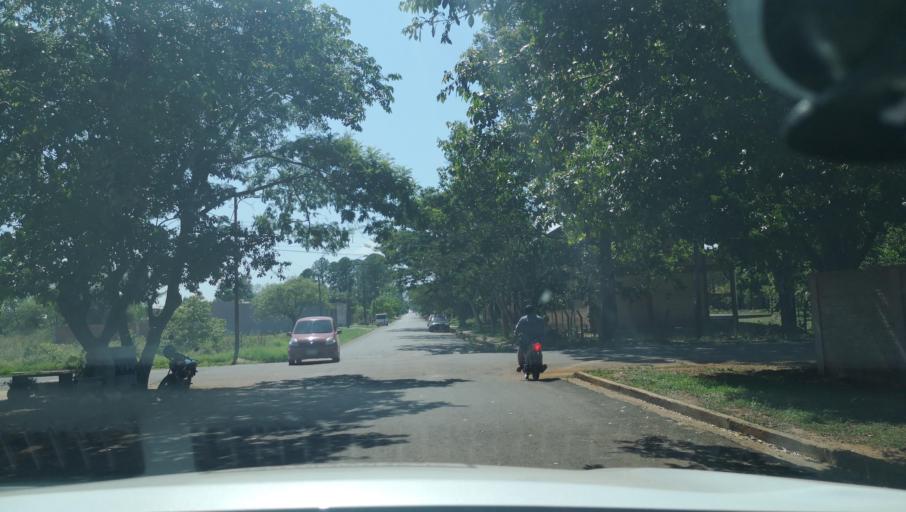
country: PY
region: Itapua
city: Carmen del Parana
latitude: -27.1596
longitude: -56.2451
